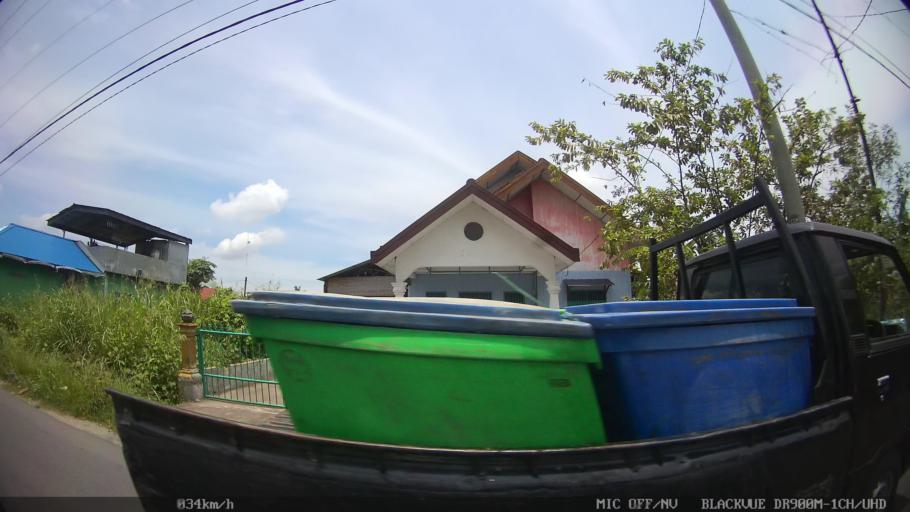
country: ID
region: North Sumatra
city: Labuhan Deli
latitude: 3.7084
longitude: 98.6774
